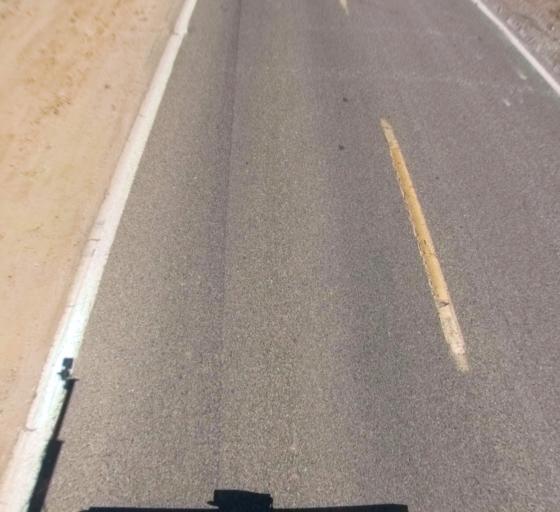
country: US
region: California
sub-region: Madera County
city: Parkwood
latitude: 36.9334
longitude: -120.0334
